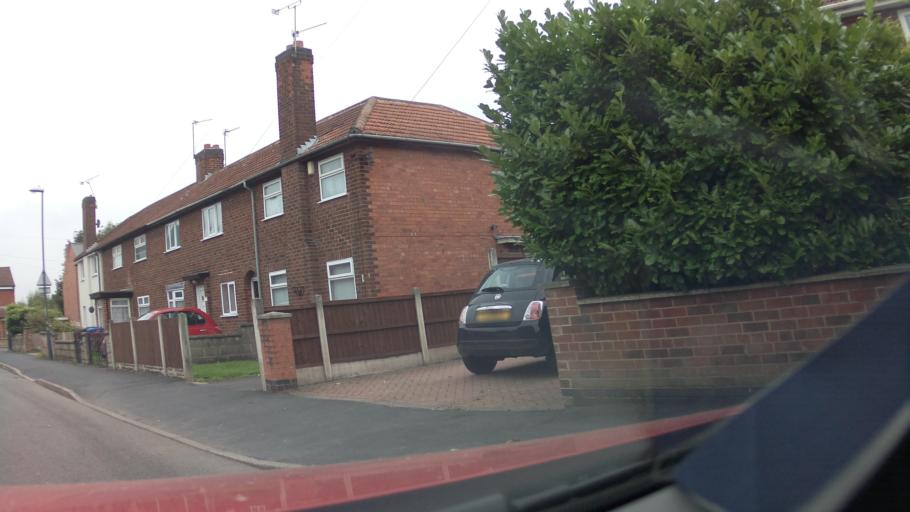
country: GB
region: England
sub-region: Derby
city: Derby
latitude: 52.9133
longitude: -1.4903
